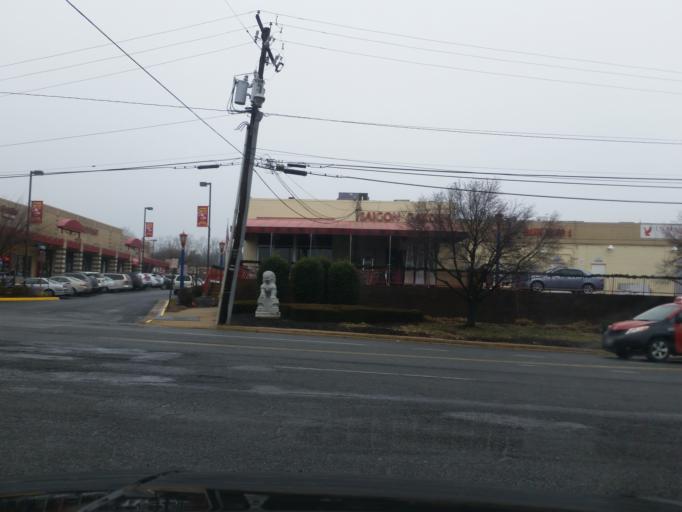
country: US
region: Virginia
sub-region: Fairfax County
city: Seven Corners
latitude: 38.8725
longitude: -77.1538
